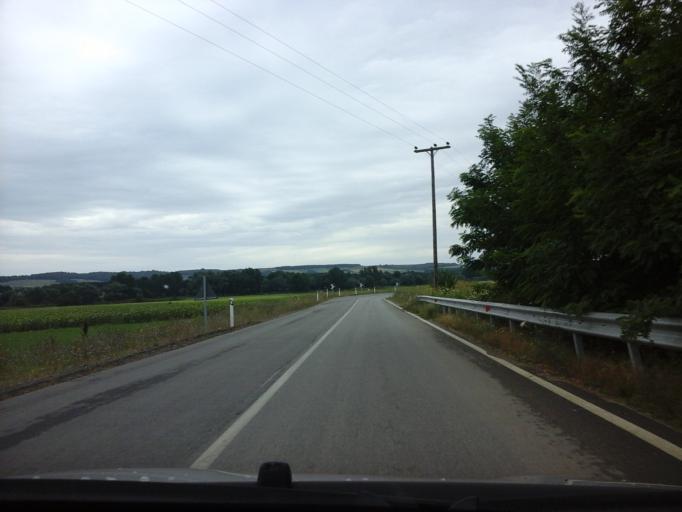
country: GR
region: East Macedonia and Thrace
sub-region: Nomos Evrou
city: Soufli
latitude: 41.1352
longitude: 26.2428
